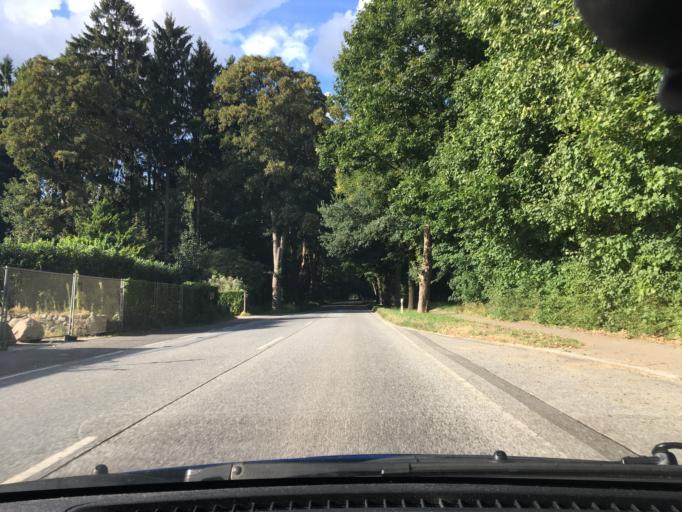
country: DE
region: Lower Saxony
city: Seevetal
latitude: 53.4214
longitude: 9.9297
